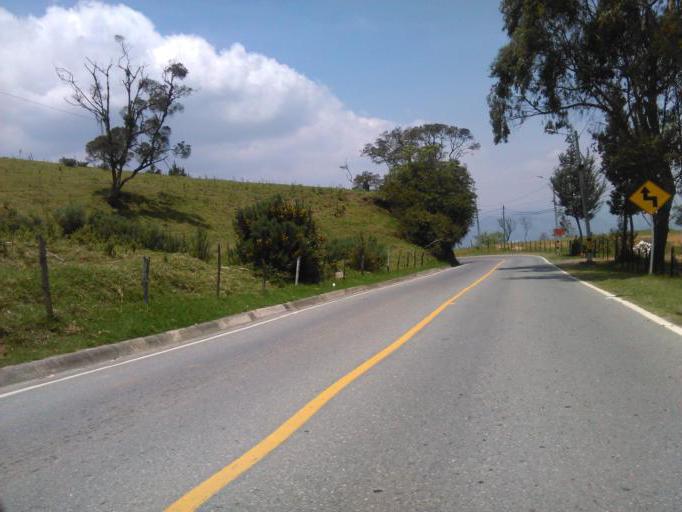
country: CO
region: Antioquia
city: La Union
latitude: 6.0010
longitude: -75.3810
